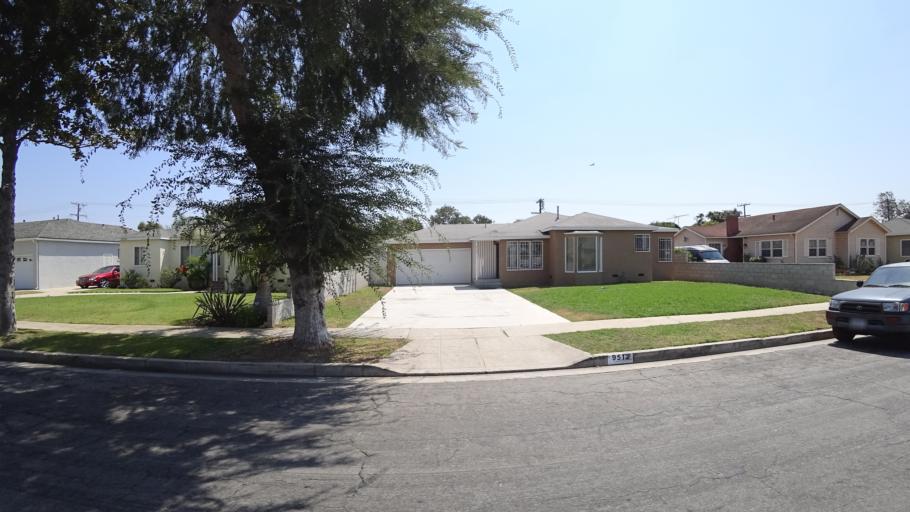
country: US
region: California
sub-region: Los Angeles County
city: Westmont
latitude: 33.9501
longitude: -118.3221
